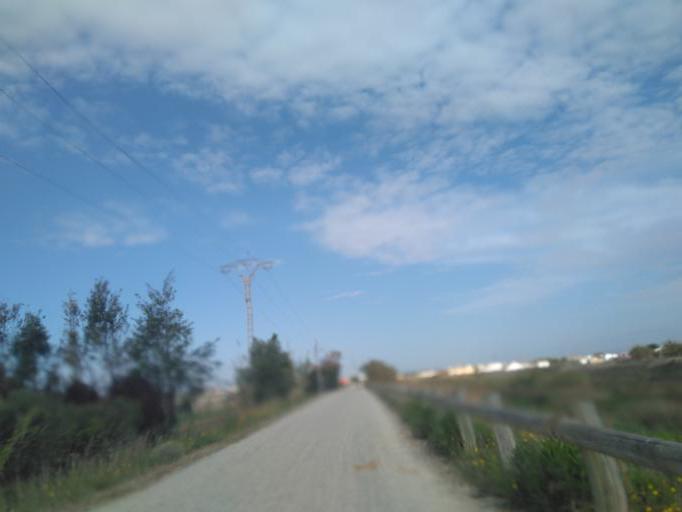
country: ES
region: Valencia
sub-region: Provincia de Valencia
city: Alboraya
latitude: 39.5028
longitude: -0.3351
